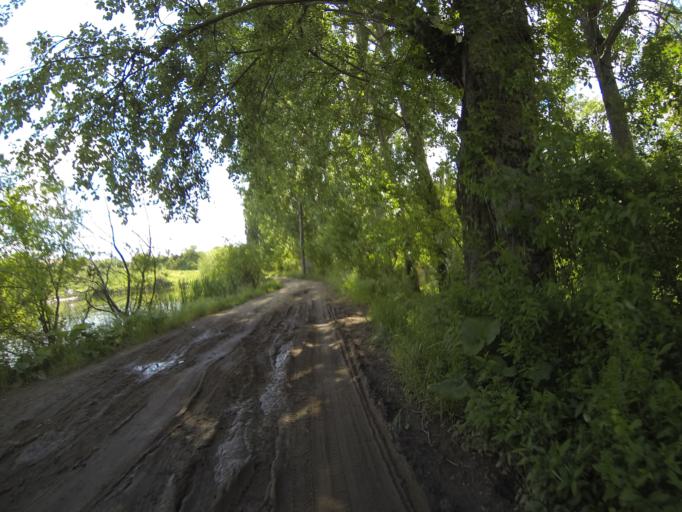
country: RO
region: Dolj
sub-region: Comuna Malu Mare
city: Preajba
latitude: 44.2695
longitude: 23.8449
